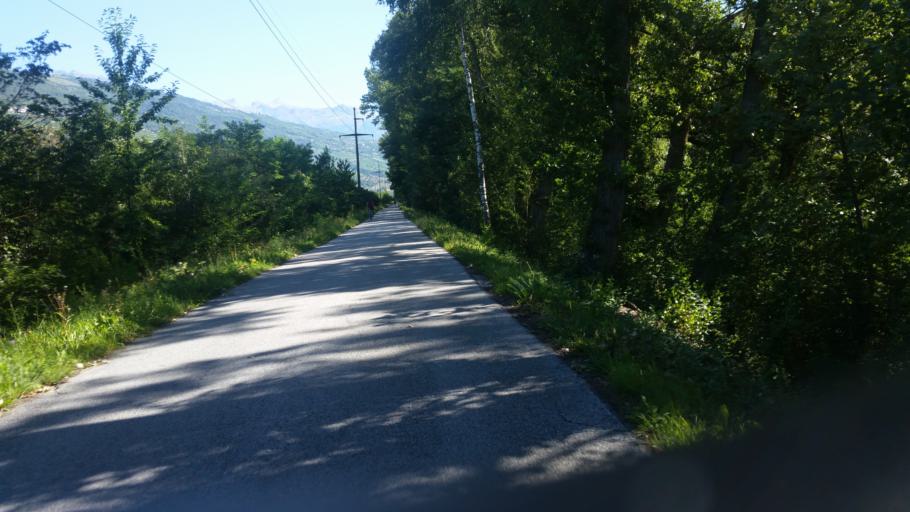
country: CH
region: Valais
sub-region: Sion District
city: Saint-Leonard
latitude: 46.2496
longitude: 7.4354
